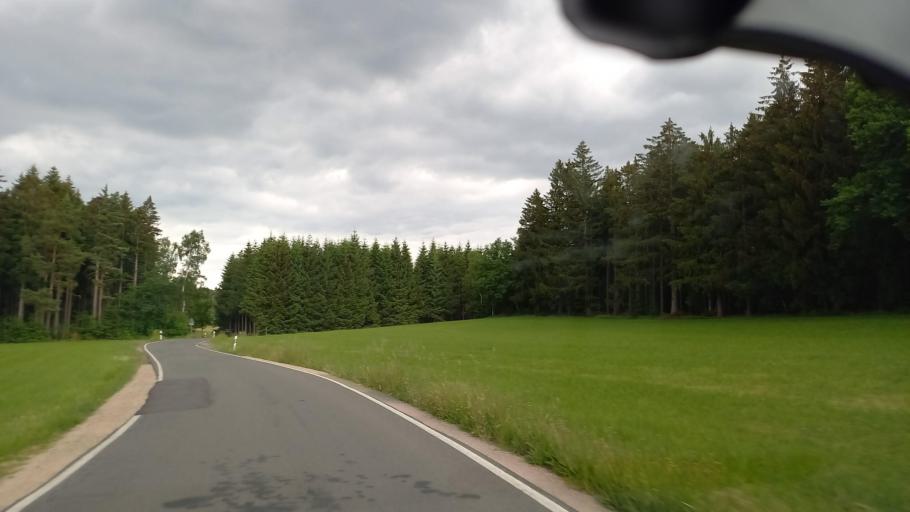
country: DE
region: Saxony
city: Rodewisch
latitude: 50.5622
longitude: 12.4536
